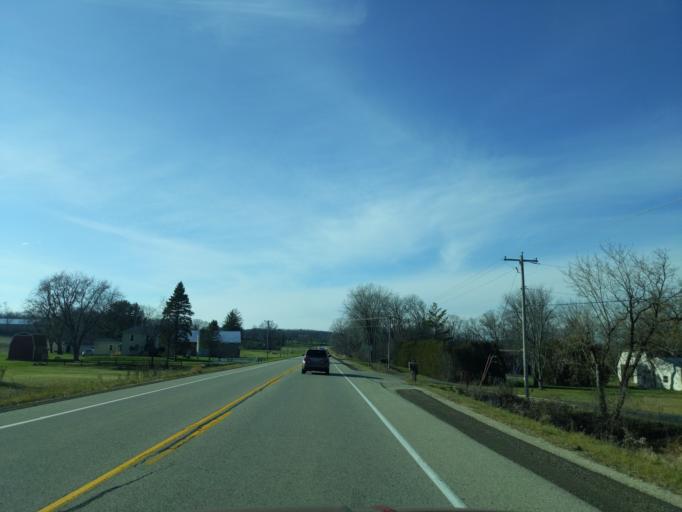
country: US
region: Wisconsin
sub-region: Rock County
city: Edgerton
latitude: 42.8273
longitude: -89.0070
